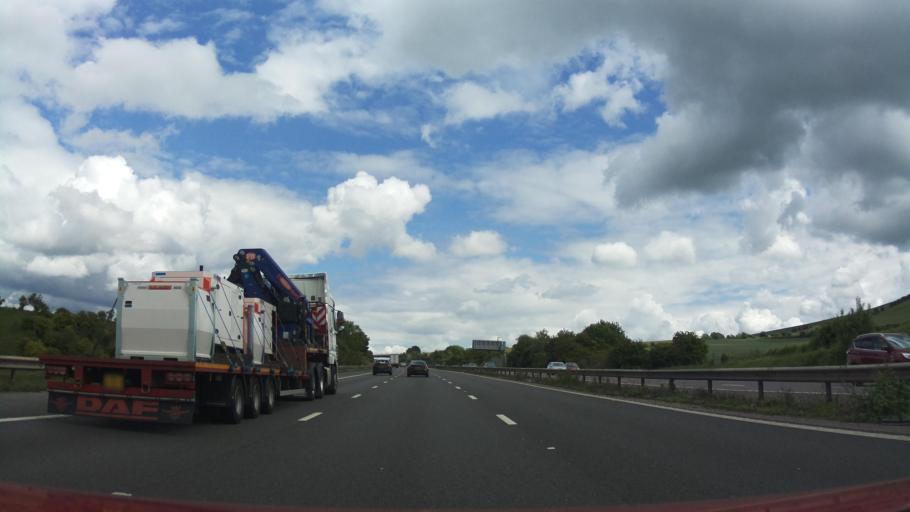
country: GB
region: England
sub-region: Borough of Swindon
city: Wanborough
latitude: 51.5259
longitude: -1.7023
